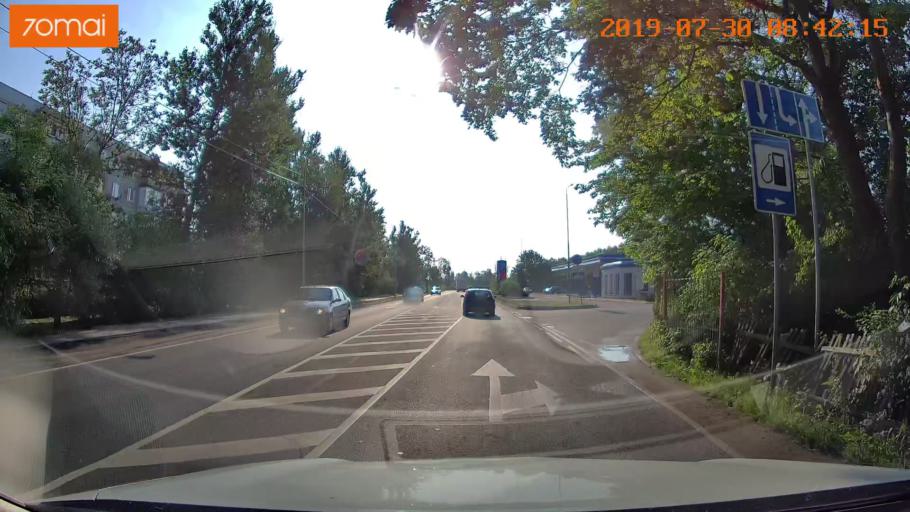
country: RU
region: Kaliningrad
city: Chernyakhovsk
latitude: 54.6297
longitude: 21.8257
